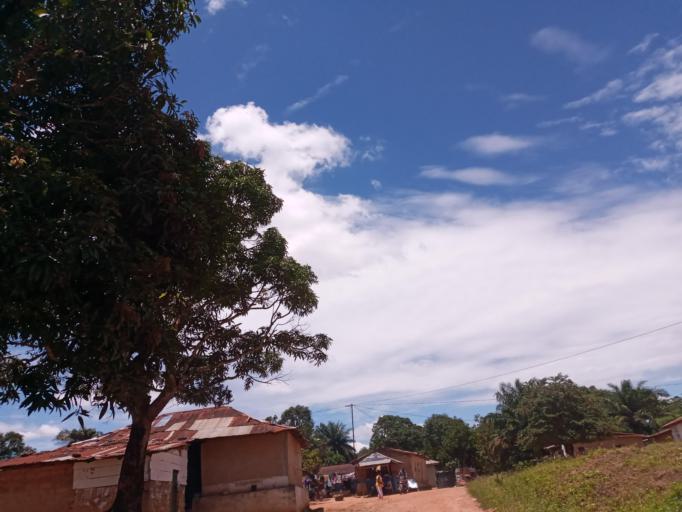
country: SL
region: Eastern Province
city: Koidu
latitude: 8.6516
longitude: -10.9608
